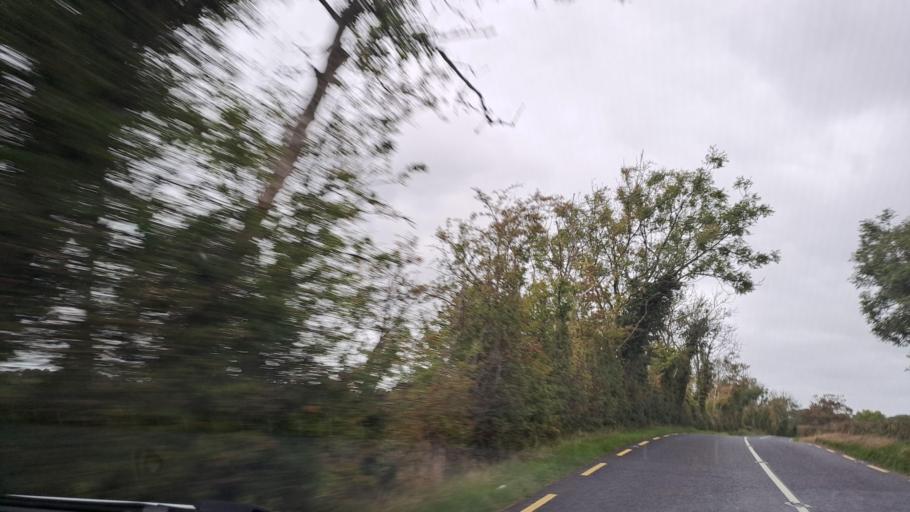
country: IE
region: Ulster
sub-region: County Monaghan
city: Monaghan
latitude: 54.1464
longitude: -6.9218
